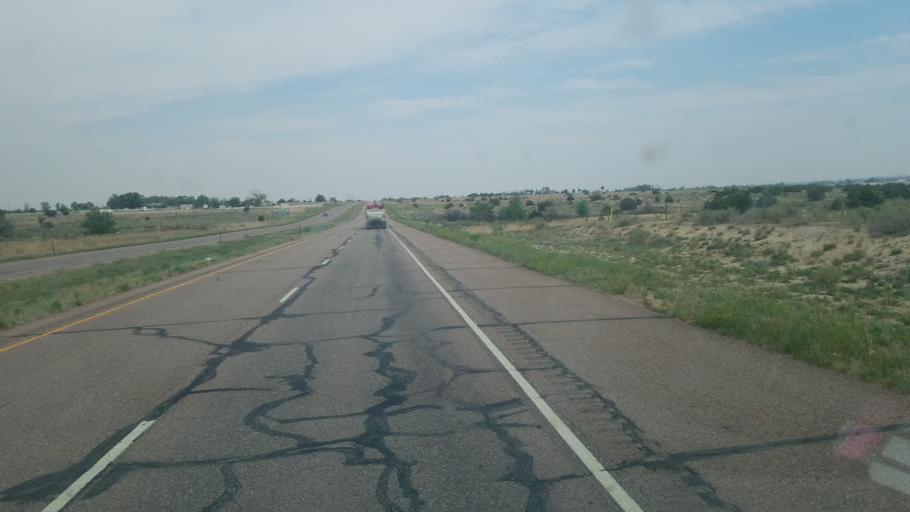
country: US
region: Colorado
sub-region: Fremont County
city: Penrose
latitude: 38.4109
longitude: -105.0127
